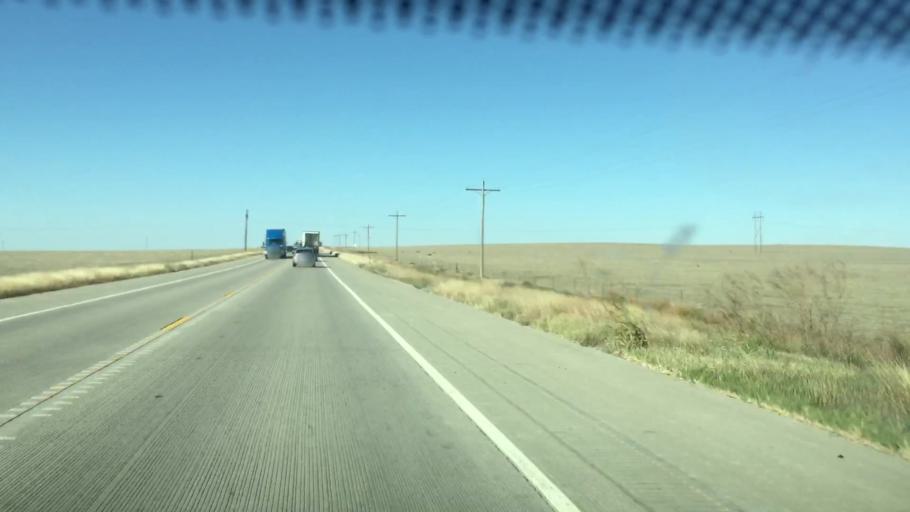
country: US
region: Colorado
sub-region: Prowers County
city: Lamar
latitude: 38.2609
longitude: -102.7239
